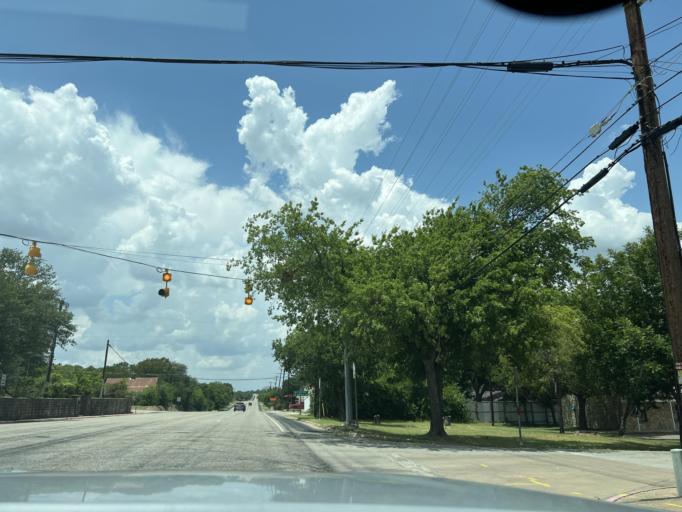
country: US
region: Texas
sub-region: Palo Pinto County
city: Palo Pinto
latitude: 32.7680
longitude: -98.2985
